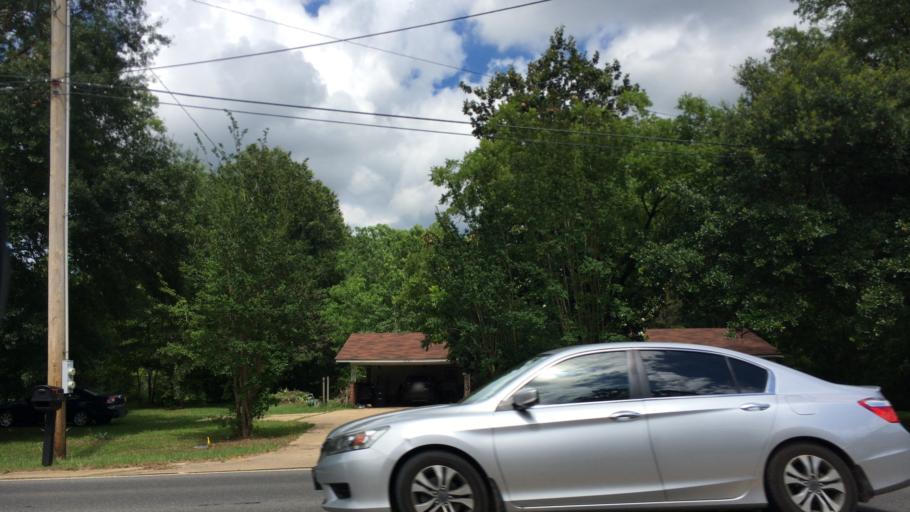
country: US
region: Louisiana
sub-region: Lincoln Parish
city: Ruston
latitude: 32.4987
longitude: -92.6368
